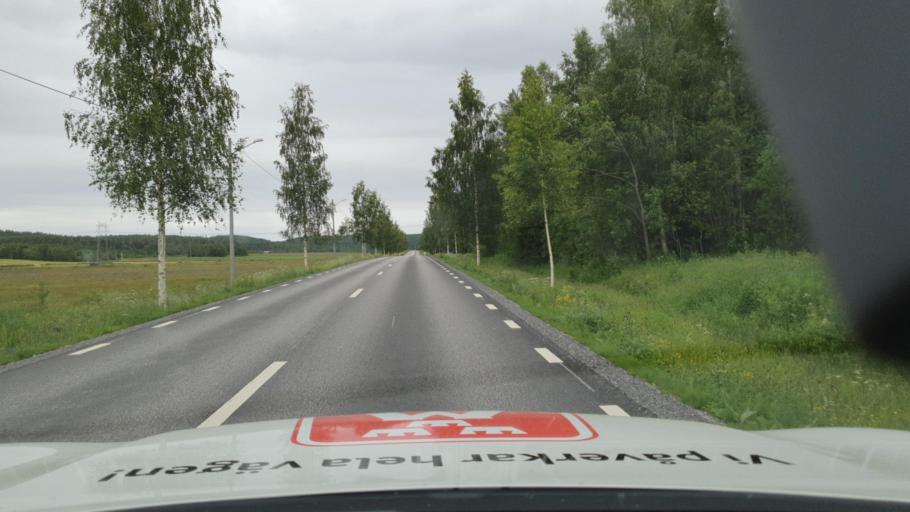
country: SE
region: Vaesterbotten
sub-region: Vannas Kommun
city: Vaennaes
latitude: 63.7480
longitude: 19.6447
